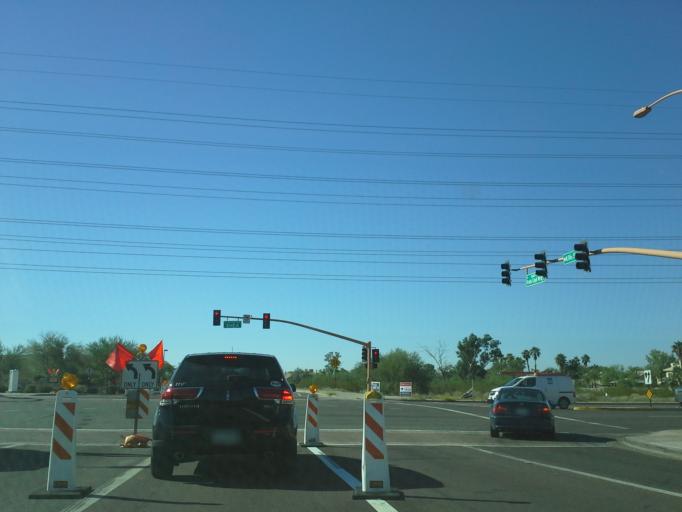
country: US
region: Arizona
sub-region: Maricopa County
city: Scottsdale
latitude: 33.5828
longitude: -111.8351
